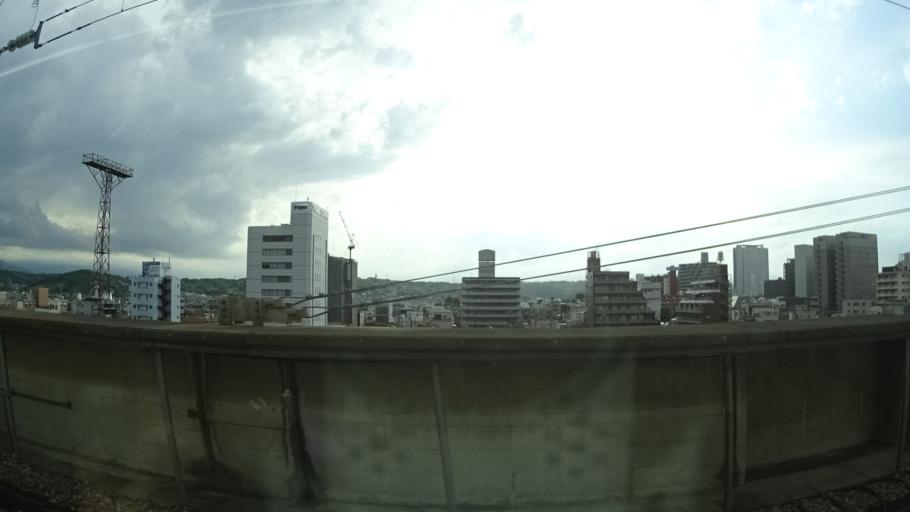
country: JP
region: Gunma
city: Takasaki
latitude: 36.3191
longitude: 139.0134
